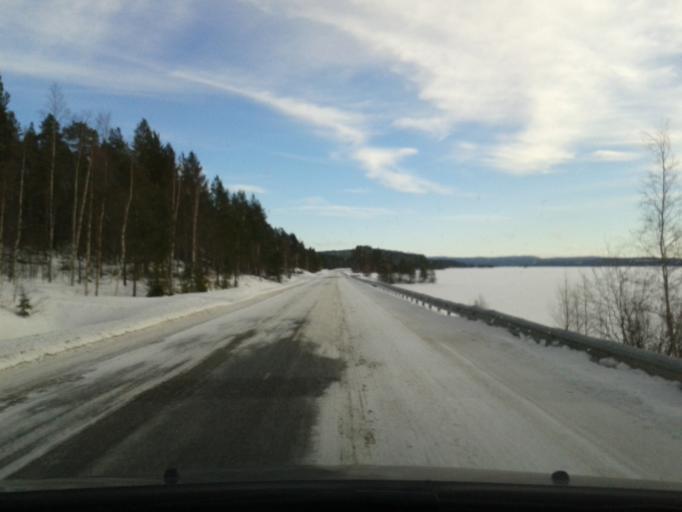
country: SE
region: Vaesterbotten
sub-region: Vilhelmina Kommun
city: Vilhelmina
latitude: 64.3905
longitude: 16.8740
